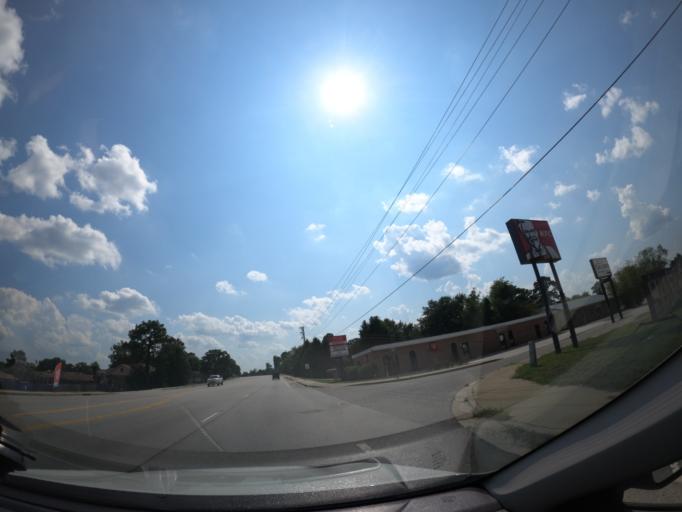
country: US
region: South Carolina
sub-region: Lexington County
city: South Congaree
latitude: 33.9377
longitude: -81.1499
